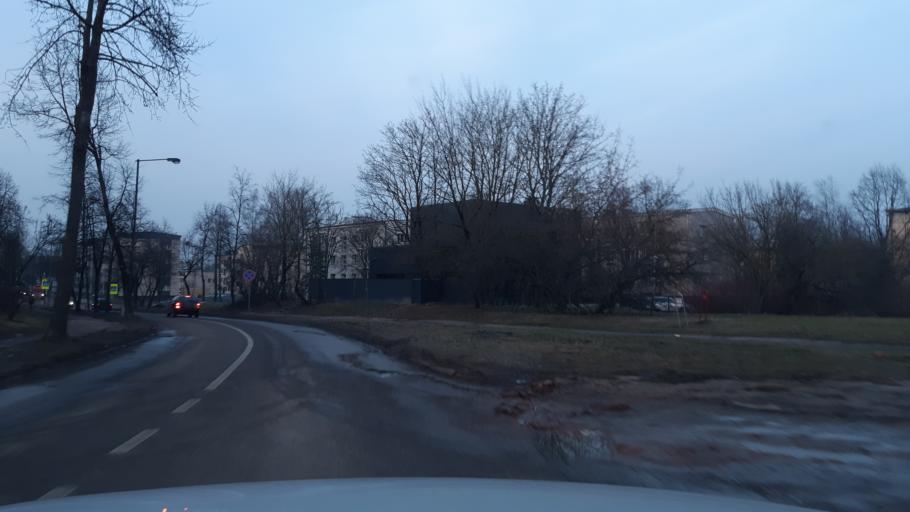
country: LT
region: Kauno apskritis
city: Dainava (Kaunas)
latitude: 54.8979
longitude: 23.9739
